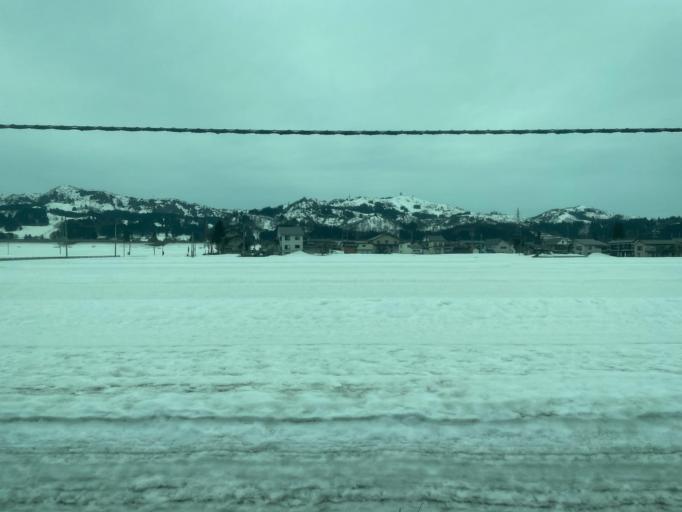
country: JP
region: Niigata
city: Shiozawa
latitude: 37.0469
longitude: 138.8580
